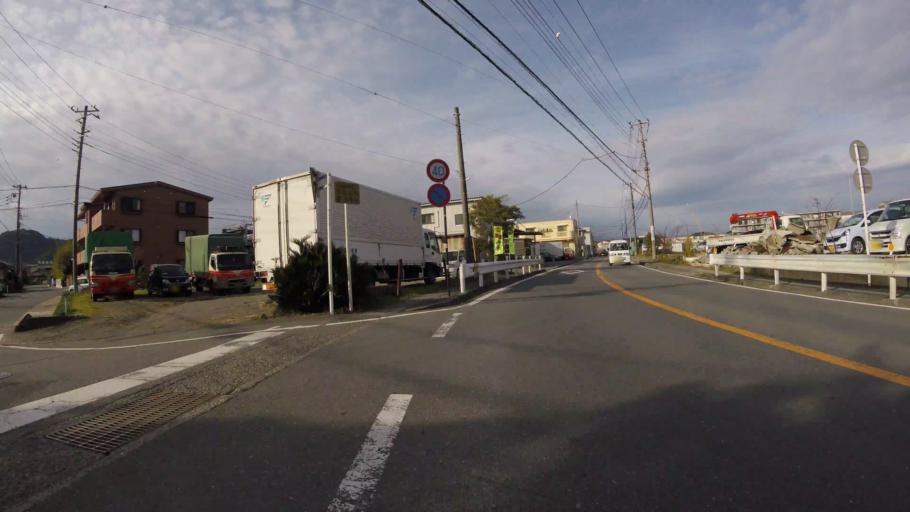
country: JP
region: Shizuoka
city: Mishima
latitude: 35.0891
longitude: 138.9089
